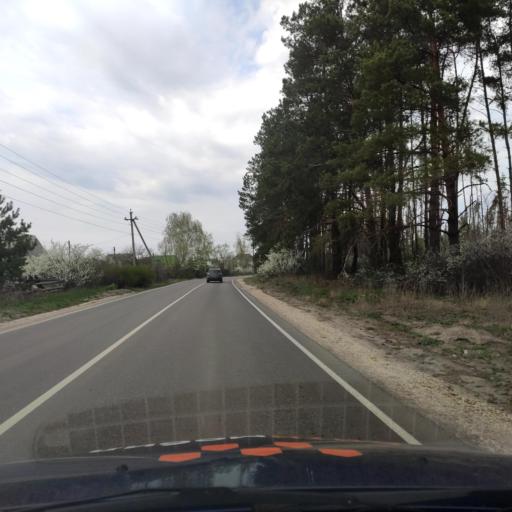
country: RU
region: Voronezj
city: Podgornoye
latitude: 51.8336
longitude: 39.1437
